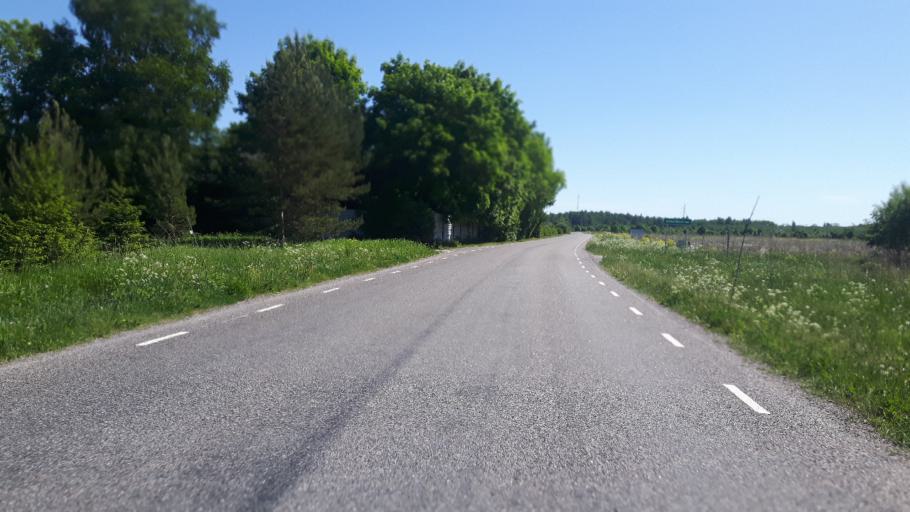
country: EE
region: Raplamaa
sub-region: Kohila vald
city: Kohila
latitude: 59.1884
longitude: 24.7109
